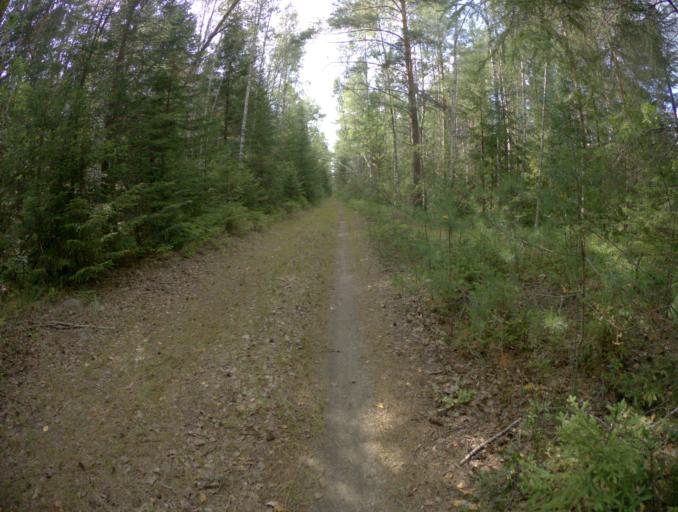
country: RU
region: Vladimir
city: Sobinka
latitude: 55.9197
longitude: 40.0770
